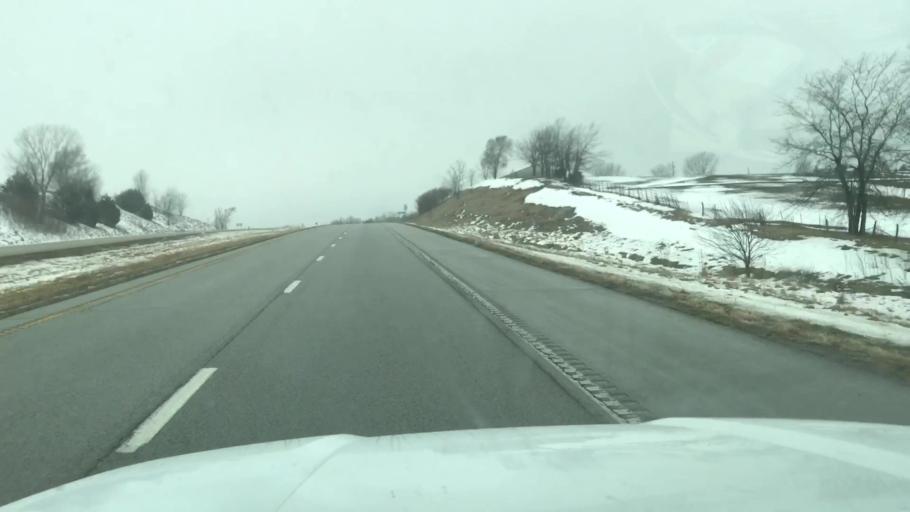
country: US
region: Missouri
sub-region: Clinton County
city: Gower
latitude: 39.7613
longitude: -94.5640
